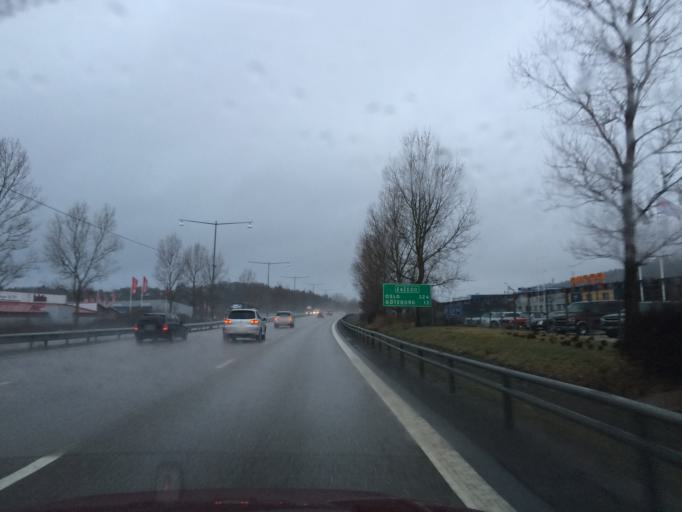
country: SE
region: Vaestra Goetaland
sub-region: Molndal
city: Kallered
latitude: 57.6077
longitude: 12.0477
